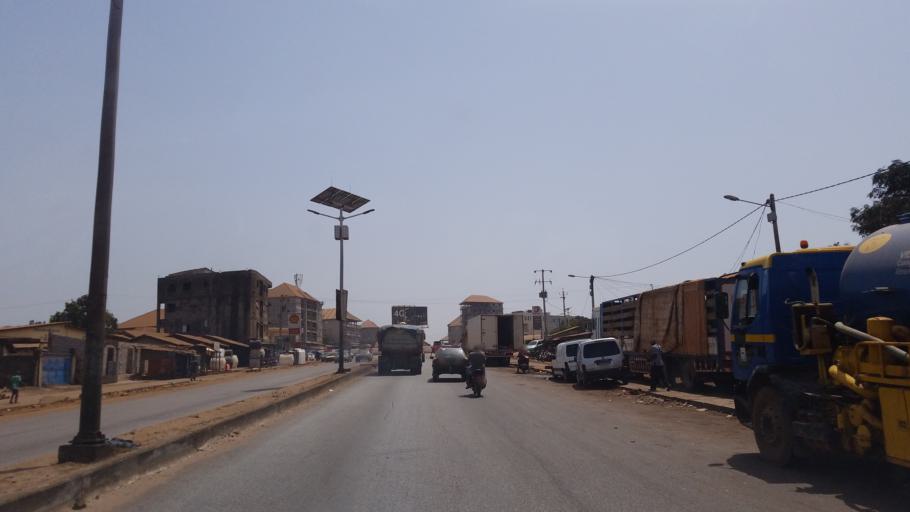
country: GN
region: Conakry
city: Conakry
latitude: 9.6440
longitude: -13.5862
